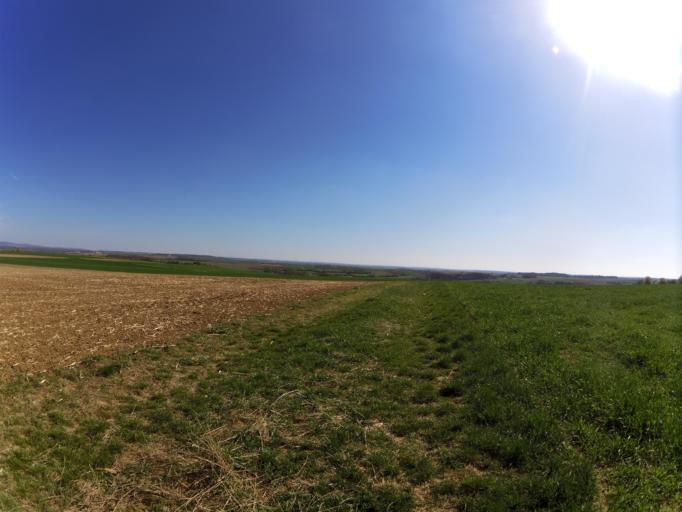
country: DE
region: Bavaria
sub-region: Regierungsbezirk Unterfranken
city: Winterhausen
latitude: 49.6845
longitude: 10.0012
